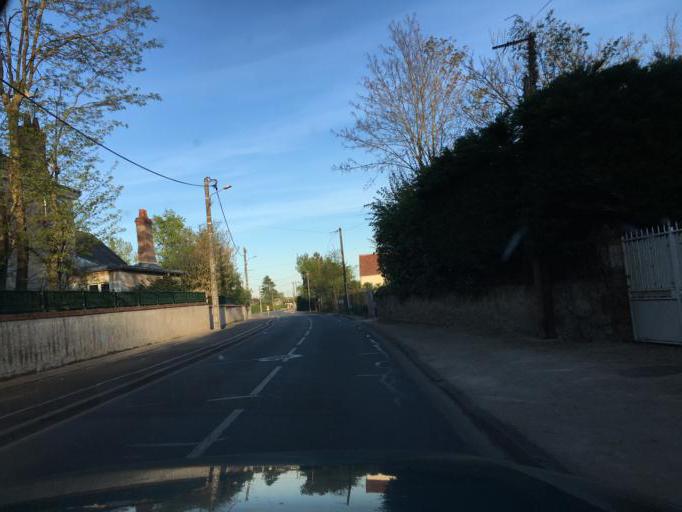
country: FR
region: Centre
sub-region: Departement du Loiret
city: Saint-Jean-le-Blanc
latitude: 47.8832
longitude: 1.9318
